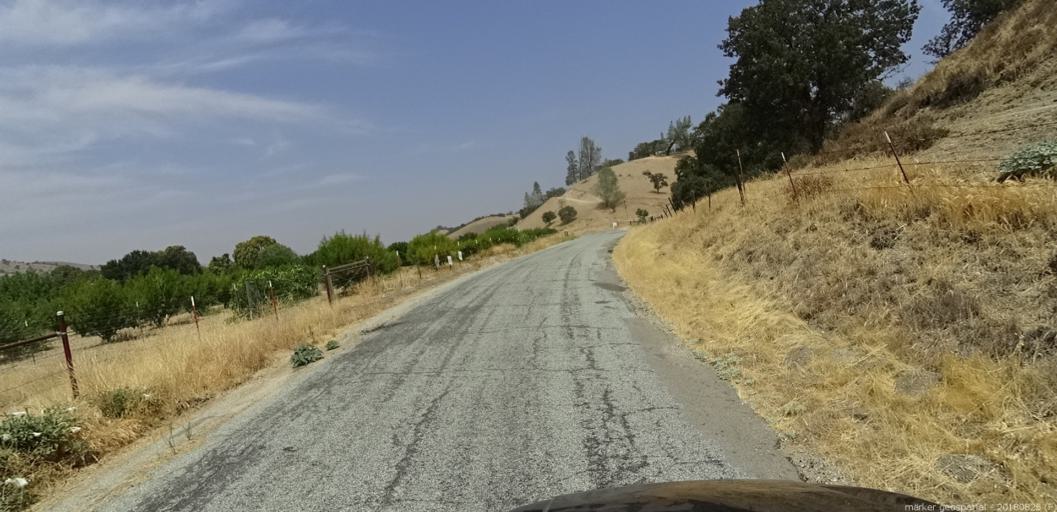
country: US
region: California
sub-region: San Luis Obispo County
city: San Miguel
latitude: 35.8712
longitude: -120.7024
